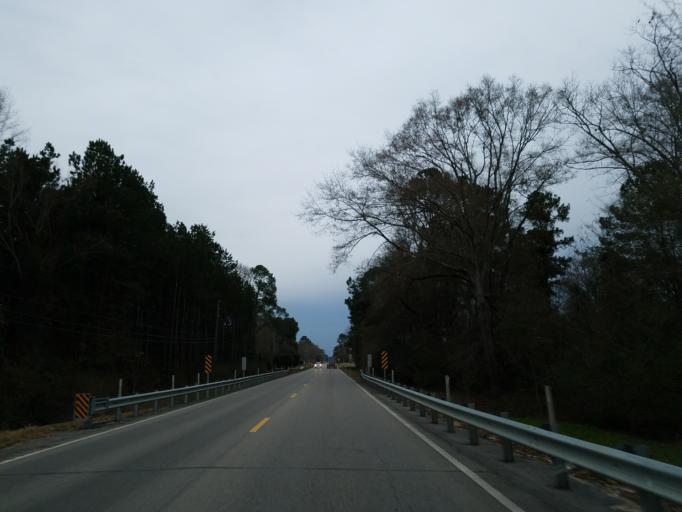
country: US
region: Mississippi
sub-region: Forrest County
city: Glendale
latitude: 31.4924
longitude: -89.2810
